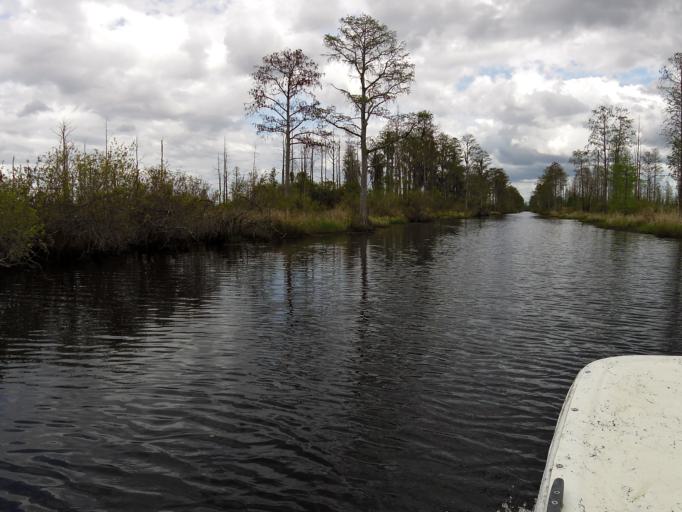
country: US
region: Georgia
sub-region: Charlton County
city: Folkston
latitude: 30.7364
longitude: -82.1648
